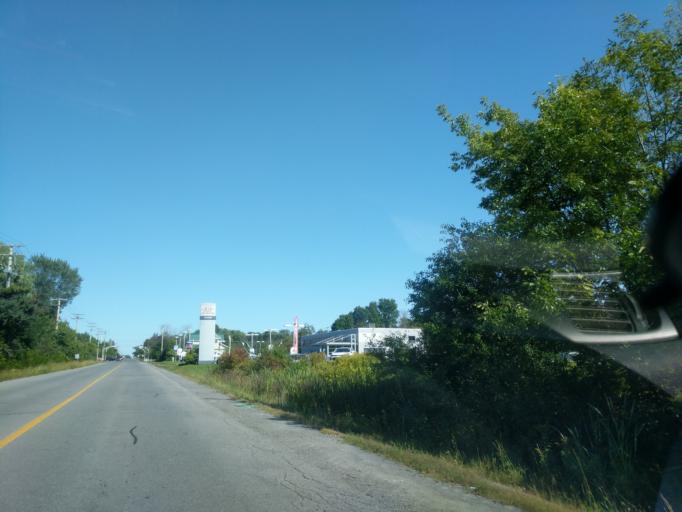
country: CA
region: Ontario
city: Bells Corners
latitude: 45.4121
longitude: -75.8114
